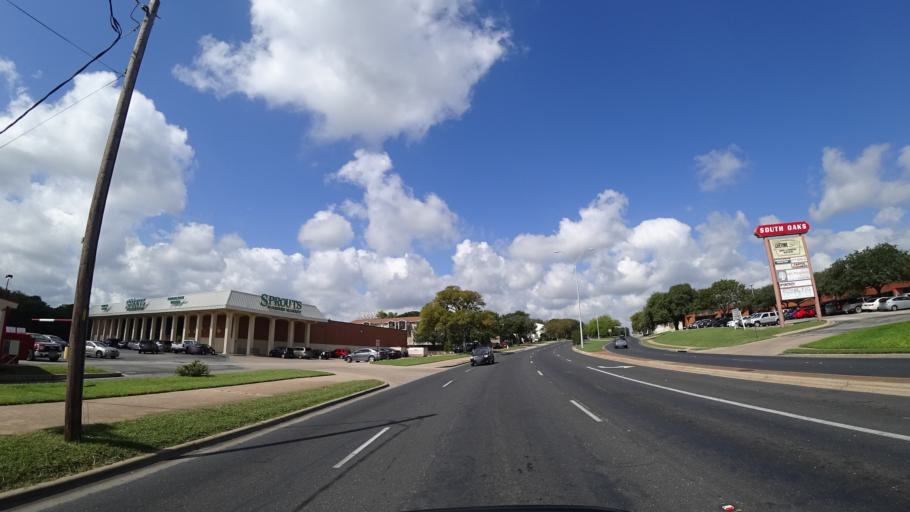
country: US
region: Texas
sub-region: Travis County
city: Shady Hollow
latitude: 30.2029
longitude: -97.8073
